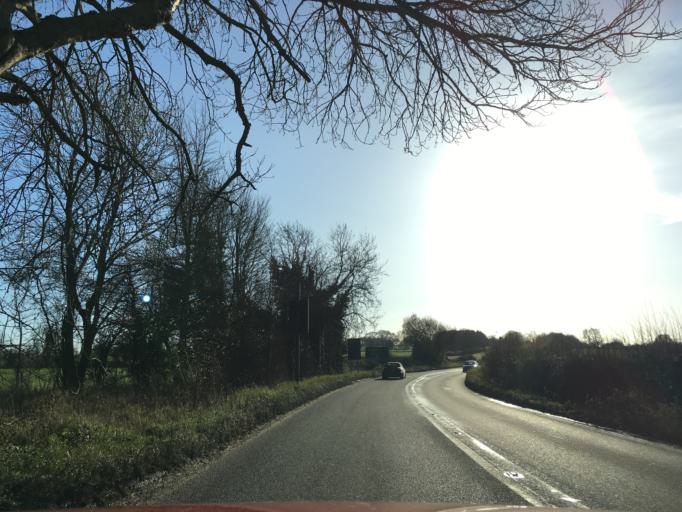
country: GB
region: England
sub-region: Wiltshire
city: Burbage
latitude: 51.3691
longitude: -1.6784
